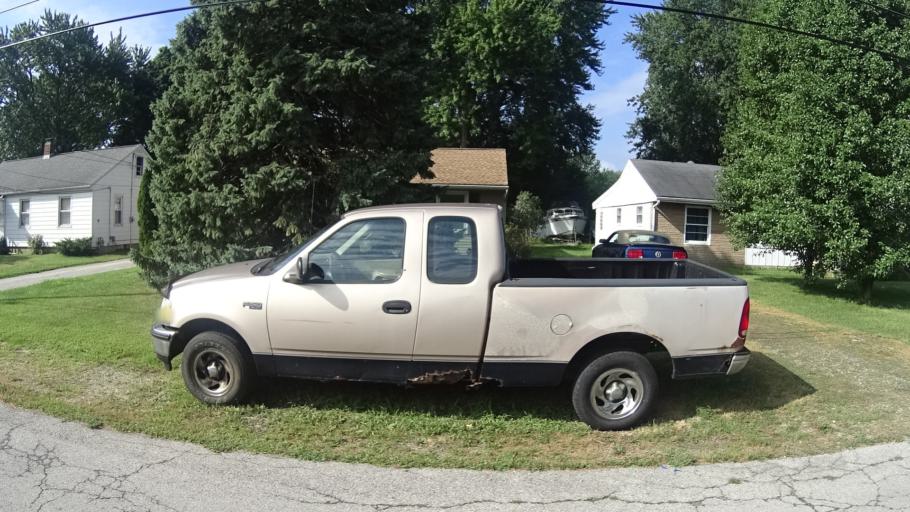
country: US
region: Ohio
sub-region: Erie County
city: Sandusky
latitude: 41.4373
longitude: -82.6743
